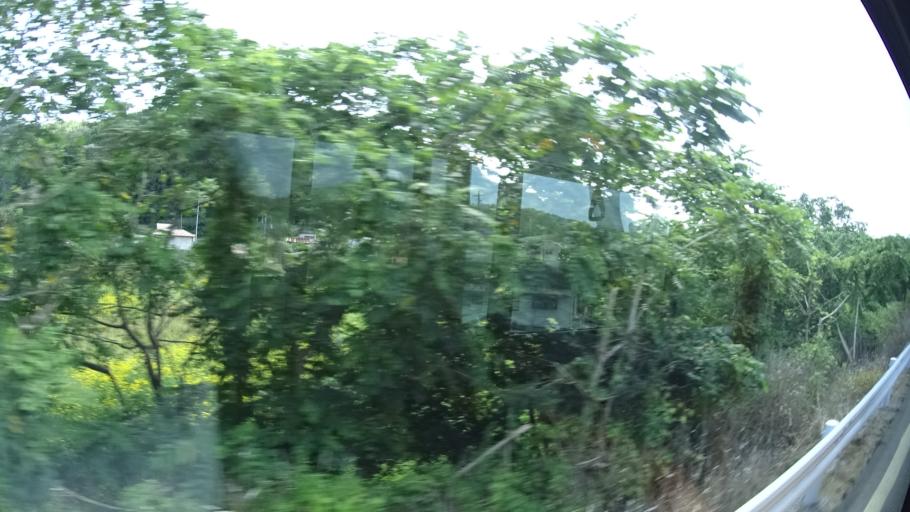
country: JP
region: Iwate
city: Ofunato
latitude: 39.0076
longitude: 141.7141
